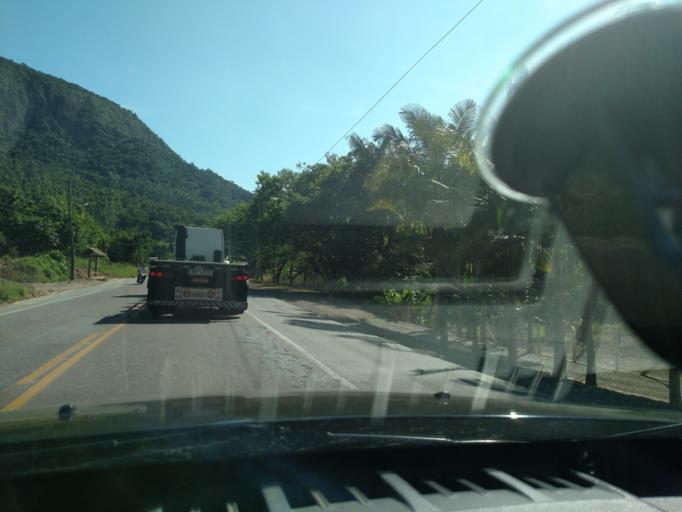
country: BR
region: Santa Catarina
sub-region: Ibirama
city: Ibirama
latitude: -27.0821
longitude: -49.4429
